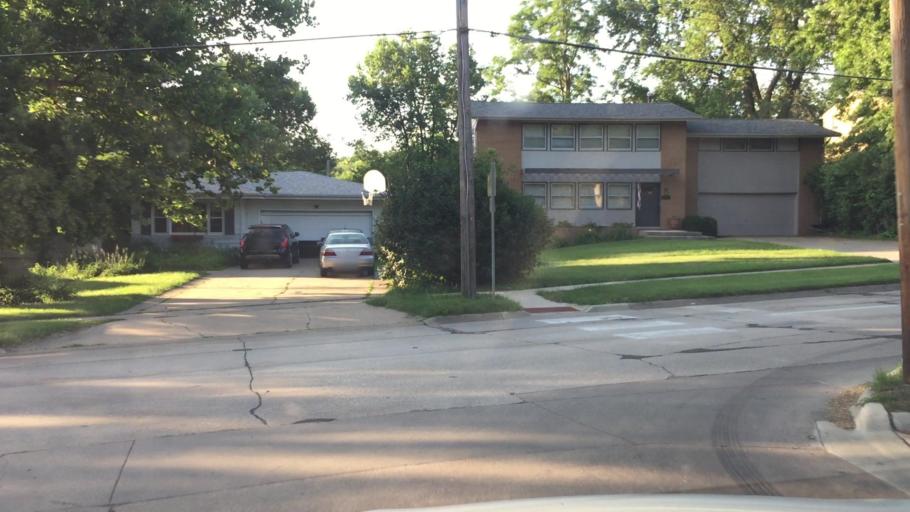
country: US
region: Iowa
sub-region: Johnson County
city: Iowa City
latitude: 41.6637
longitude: -91.5074
